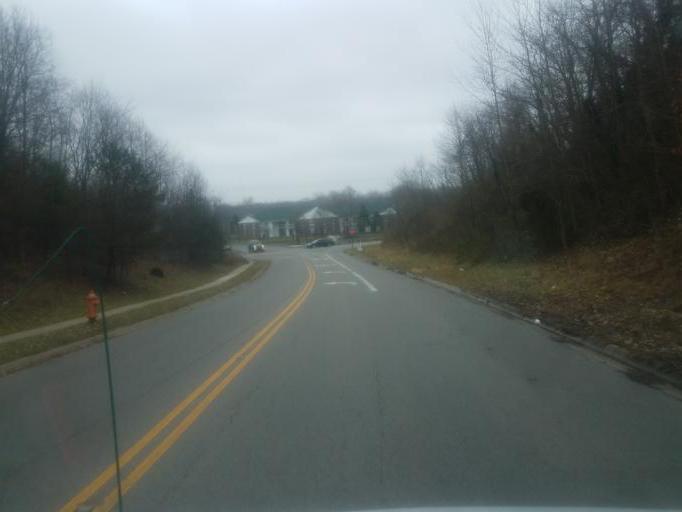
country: US
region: Ohio
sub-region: Franklin County
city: Minerva Park
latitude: 40.0904
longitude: -82.9363
